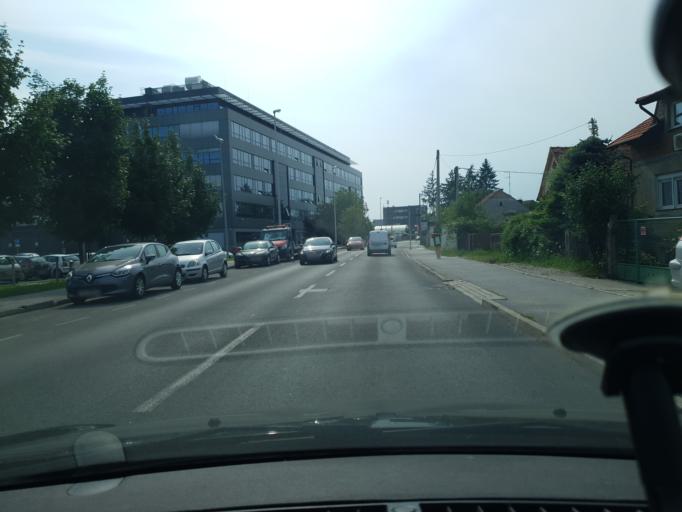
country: HR
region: Grad Zagreb
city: Stenjevec
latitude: 45.8118
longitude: 15.8656
